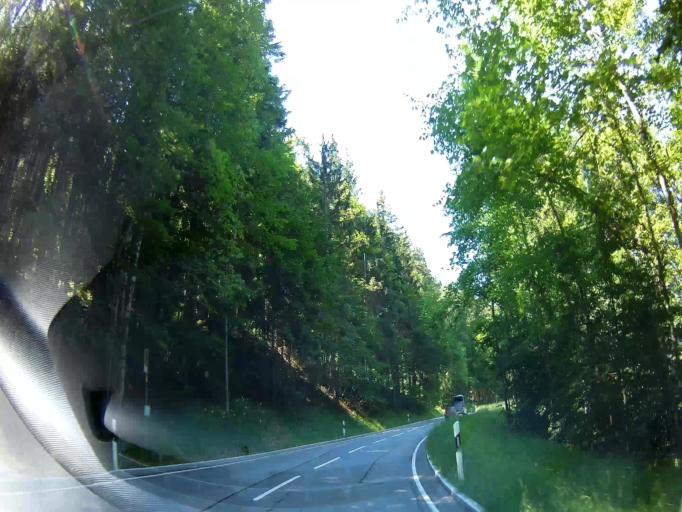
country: AT
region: Salzburg
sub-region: Politischer Bezirk Hallein
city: Hallein
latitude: 47.6415
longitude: 13.0620
